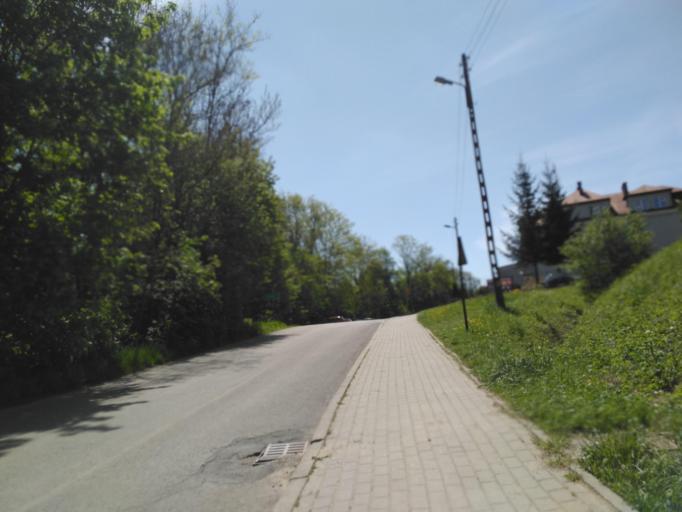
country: PL
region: Subcarpathian Voivodeship
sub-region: Powiat krosnienski
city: Iwonicz-Zdroj
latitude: 49.5412
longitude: 21.7623
